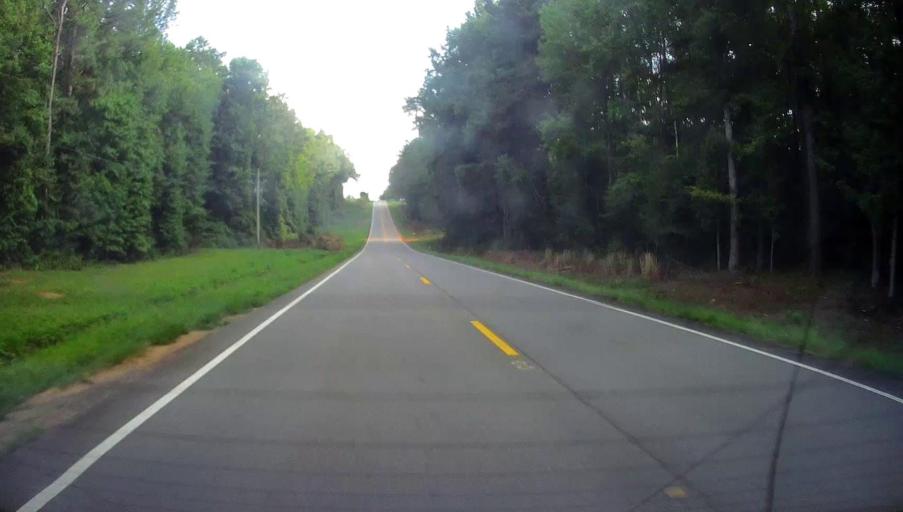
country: US
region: Georgia
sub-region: Monroe County
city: Forsyth
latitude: 32.9742
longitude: -83.9541
